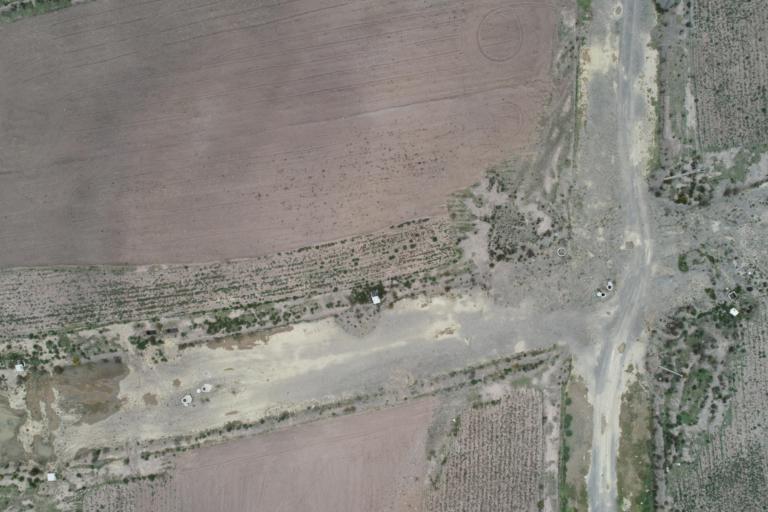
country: BO
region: La Paz
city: La Paz
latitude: -16.5143
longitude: -68.3022
